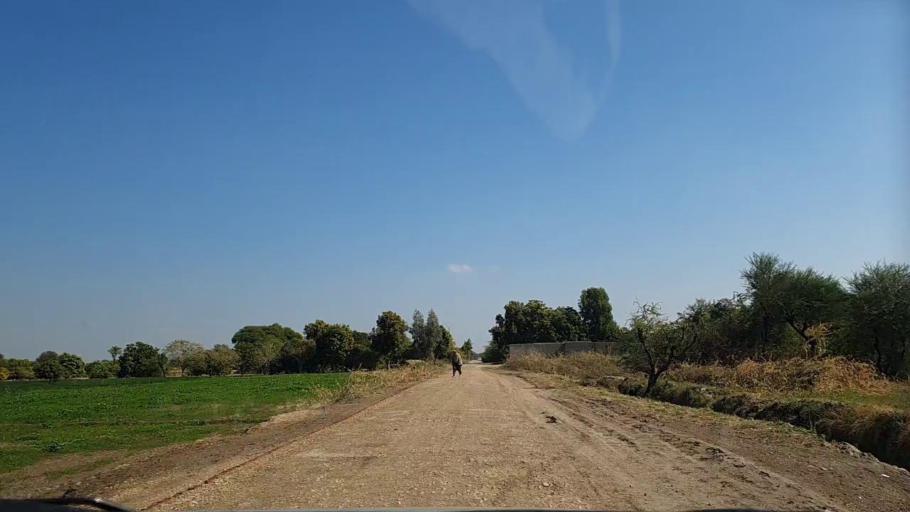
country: PK
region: Sindh
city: Pithoro
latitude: 25.6959
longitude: 69.3519
